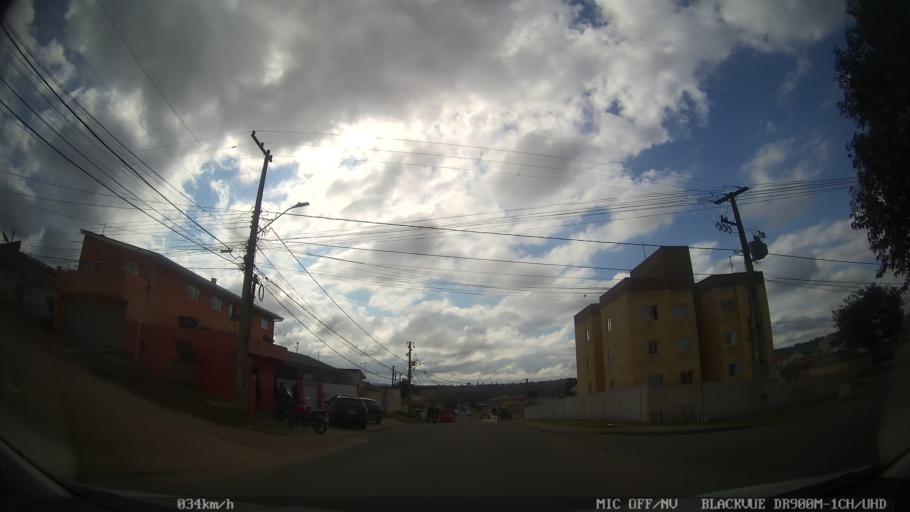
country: BR
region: Parana
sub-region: Colombo
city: Colombo
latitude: -25.3489
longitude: -49.1939
